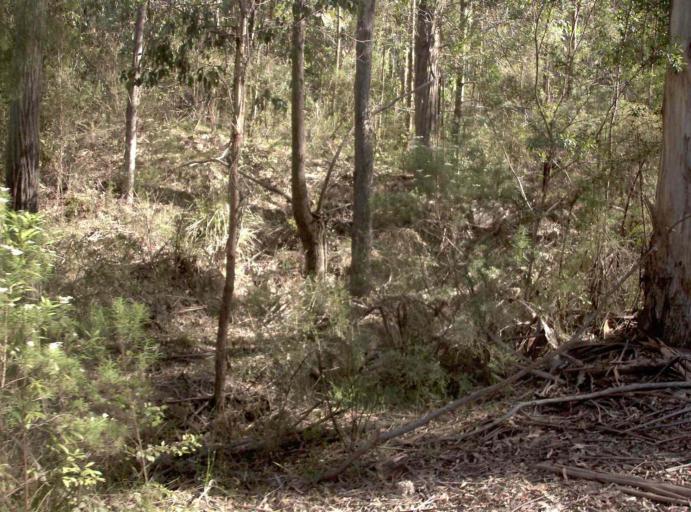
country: AU
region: Victoria
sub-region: East Gippsland
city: Lakes Entrance
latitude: -37.4582
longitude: 148.5701
